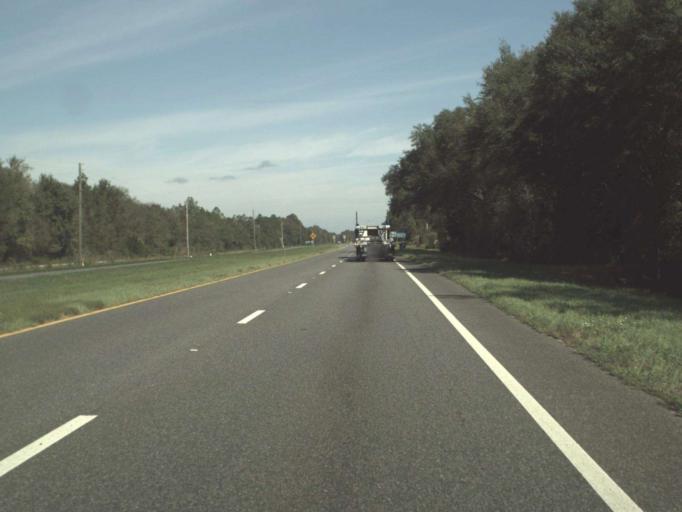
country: US
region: Florida
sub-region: Washington County
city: Chipley
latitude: 30.7081
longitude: -85.3910
